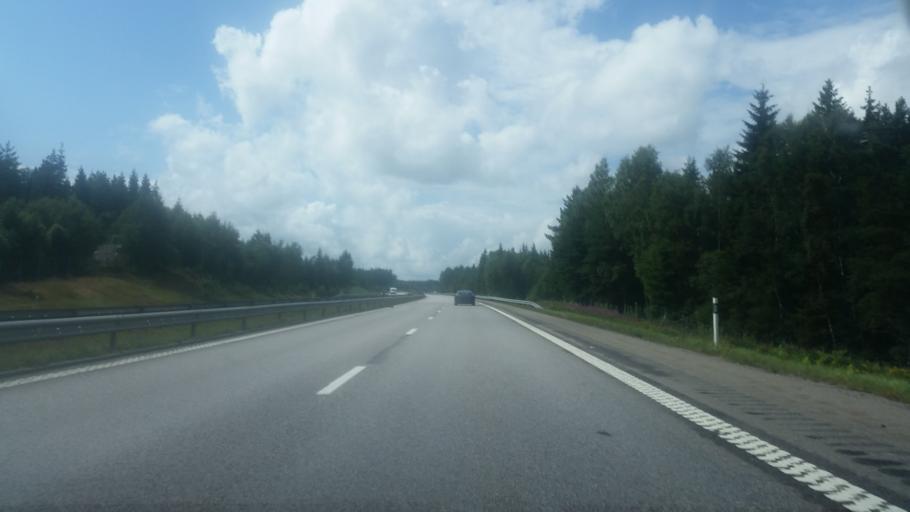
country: SE
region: Vaestra Goetaland
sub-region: Boras Kommun
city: Sandared
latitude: 57.6829
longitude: 12.7465
